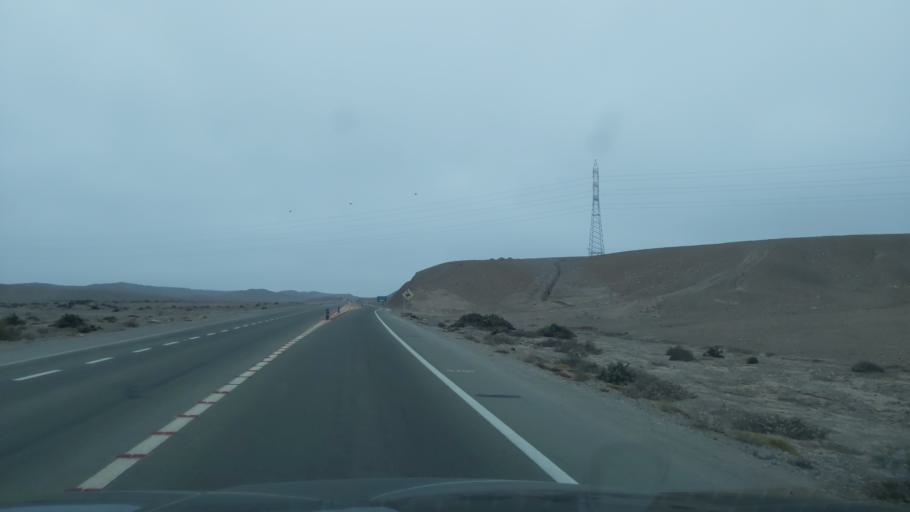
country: CL
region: Atacama
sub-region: Provincia de Copiapo
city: Copiapo
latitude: -27.2899
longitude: -70.1479
